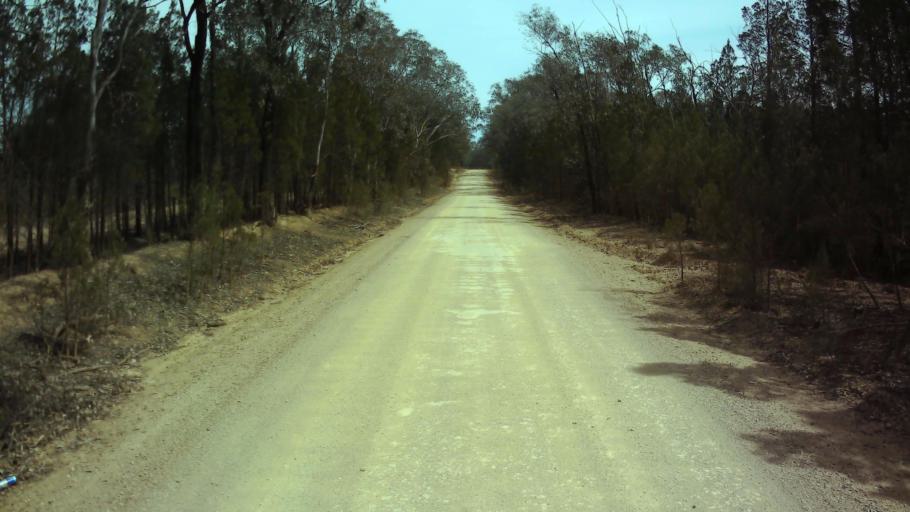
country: AU
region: New South Wales
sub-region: Weddin
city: Grenfell
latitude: -33.9082
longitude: 148.4102
